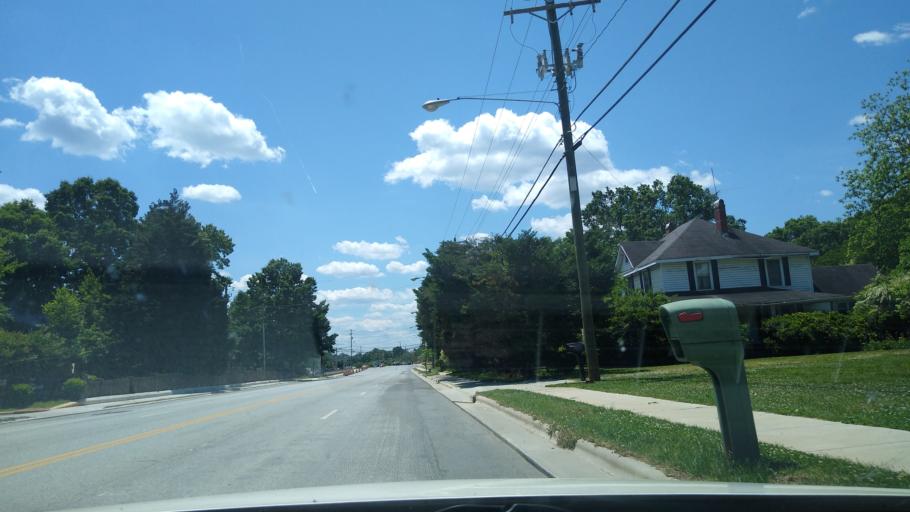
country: US
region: North Carolina
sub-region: Guilford County
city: Jamestown
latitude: 36.0794
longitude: -79.8954
